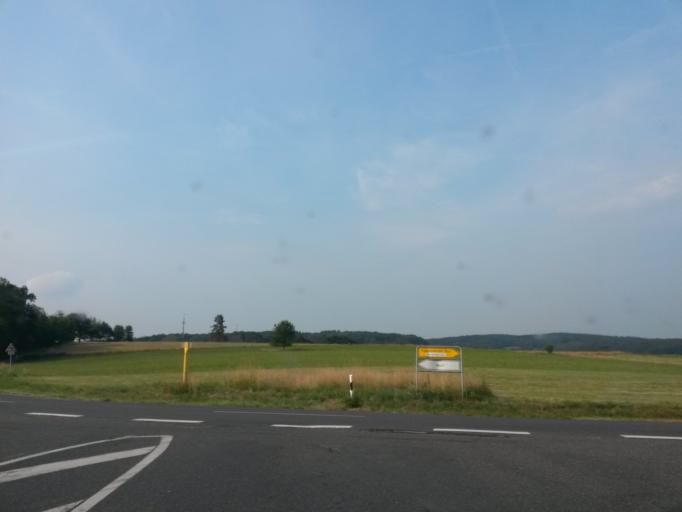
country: DE
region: North Rhine-Westphalia
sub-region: Regierungsbezirk Koln
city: Much
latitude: 50.8945
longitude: 7.4209
